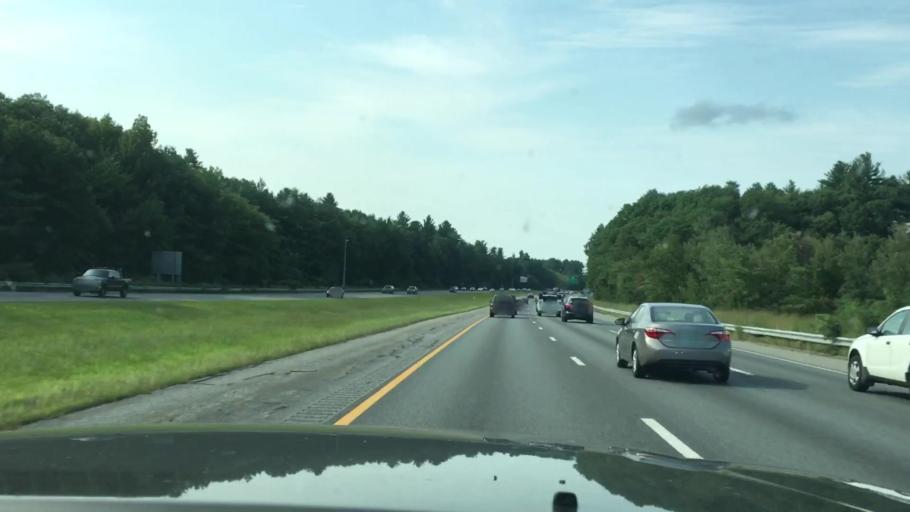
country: US
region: Massachusetts
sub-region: Middlesex County
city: Tyngsboro
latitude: 42.6691
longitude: -71.4364
